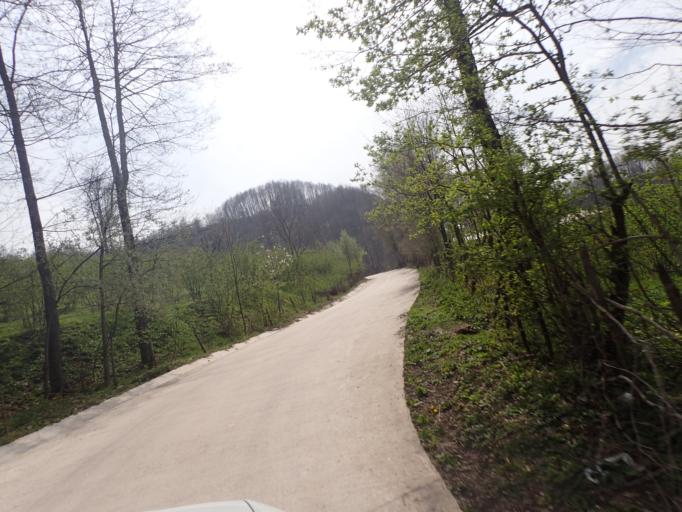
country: TR
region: Ordu
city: Aybasti
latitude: 40.7109
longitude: 37.2862
